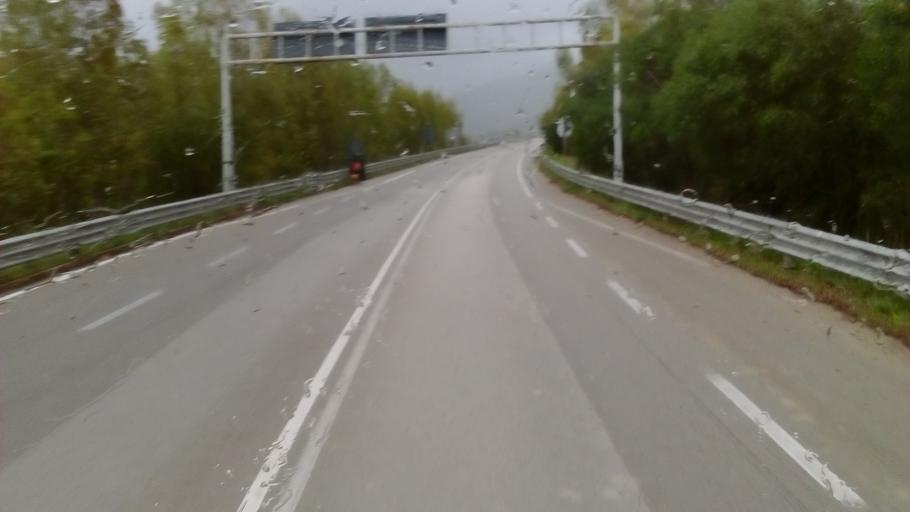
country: IT
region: Sicily
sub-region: Enna
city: Villarosa
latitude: 37.5343
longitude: 14.1298
